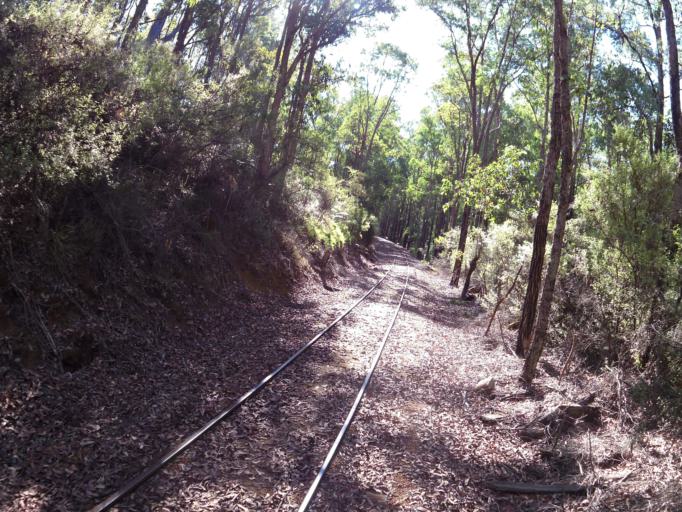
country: AU
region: Western Australia
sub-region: Waroona
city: Waroona
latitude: -32.7240
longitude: 116.1090
